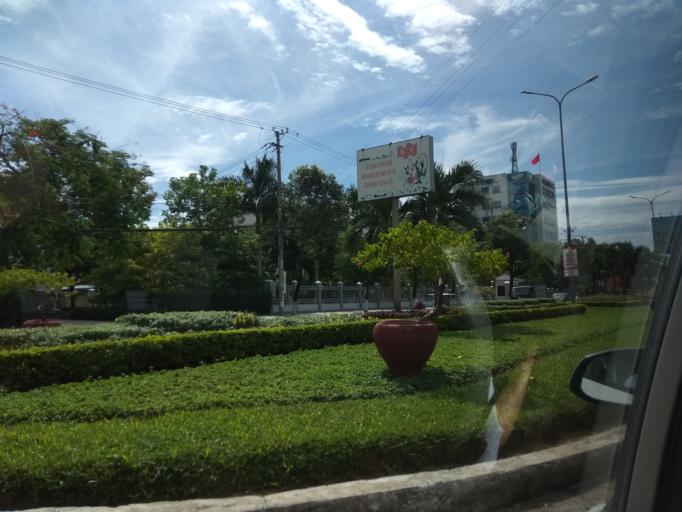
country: VN
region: Quang Nam
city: Tam Ky
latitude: 15.5698
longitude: 108.4748
